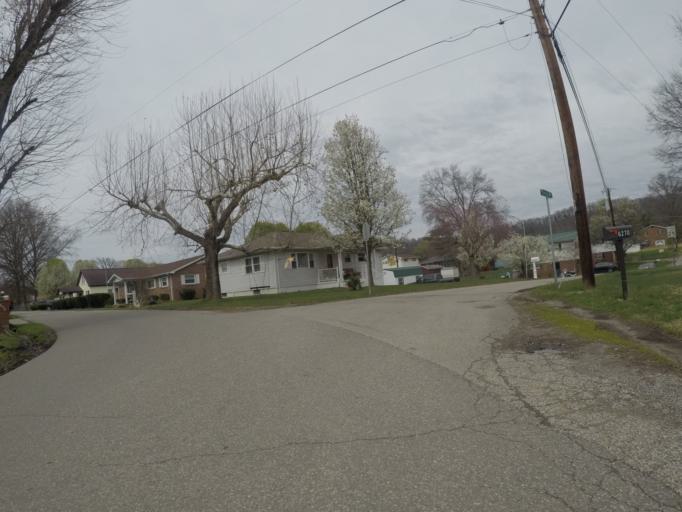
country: US
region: West Virginia
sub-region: Cabell County
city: Barboursville
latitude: 38.4219
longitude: -82.3048
